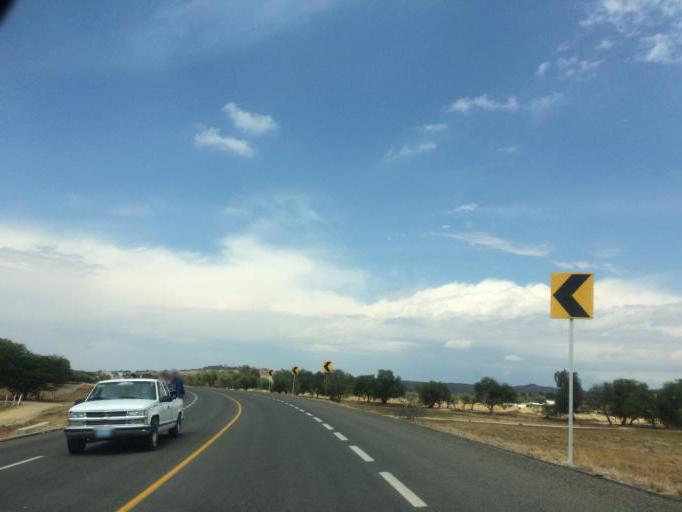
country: MX
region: Guanajuato
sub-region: Silao de la Victoria
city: Loma de Yerbabuena
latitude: 21.0325
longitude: -101.4619
